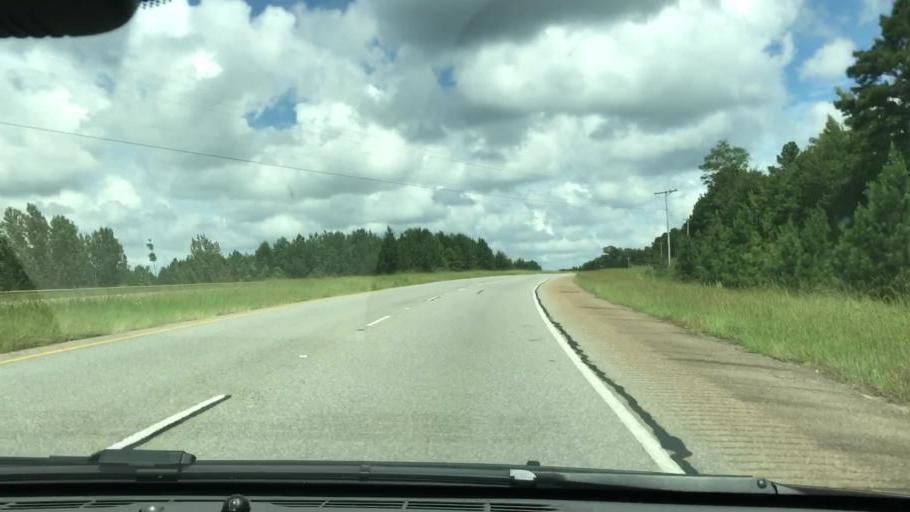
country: US
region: Georgia
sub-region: Stewart County
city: Lumpkin
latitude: 32.1112
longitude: -84.8140
